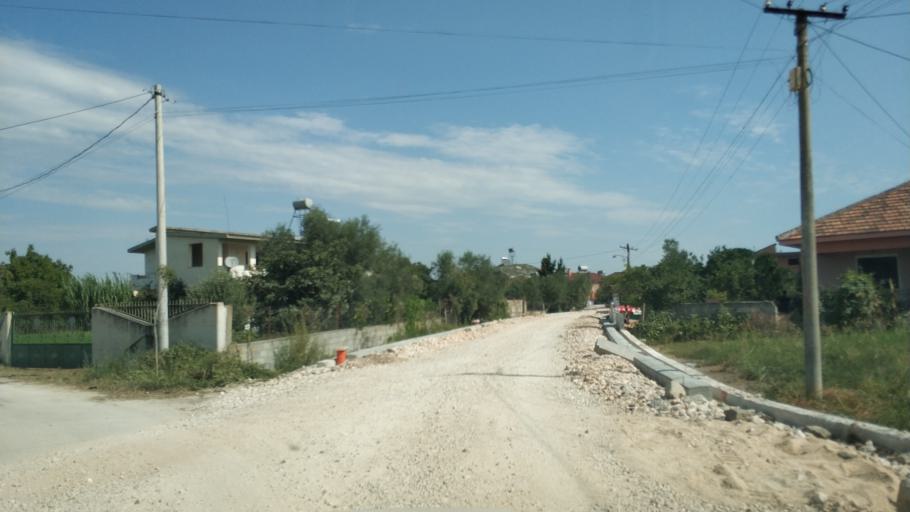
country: AL
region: Fier
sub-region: Rrethi i Lushnjes
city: Divjake
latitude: 40.9930
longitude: 19.5262
